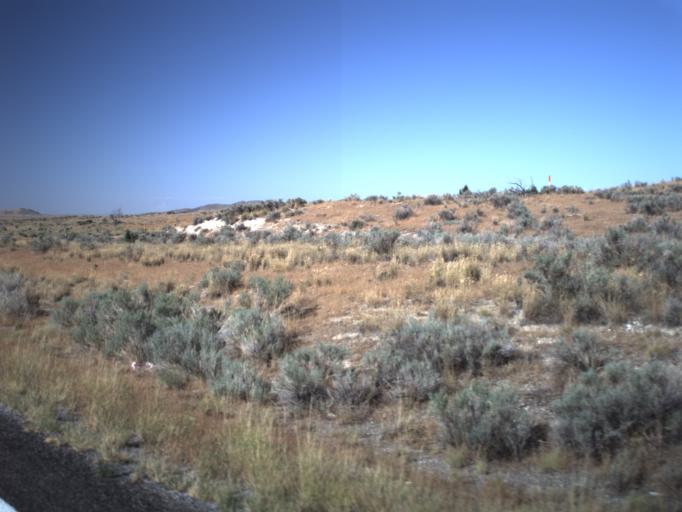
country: US
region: Utah
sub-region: Juab County
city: Mona
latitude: 39.7476
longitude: -112.1852
